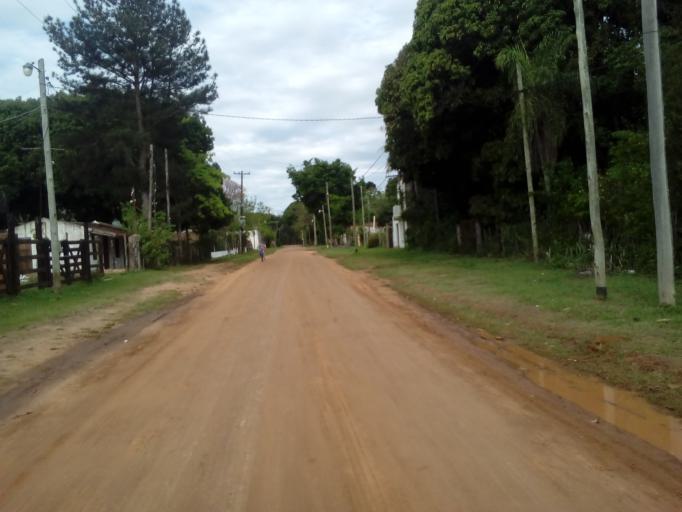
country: AR
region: Corrientes
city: San Luis del Palmar
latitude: -27.4561
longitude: -58.6529
